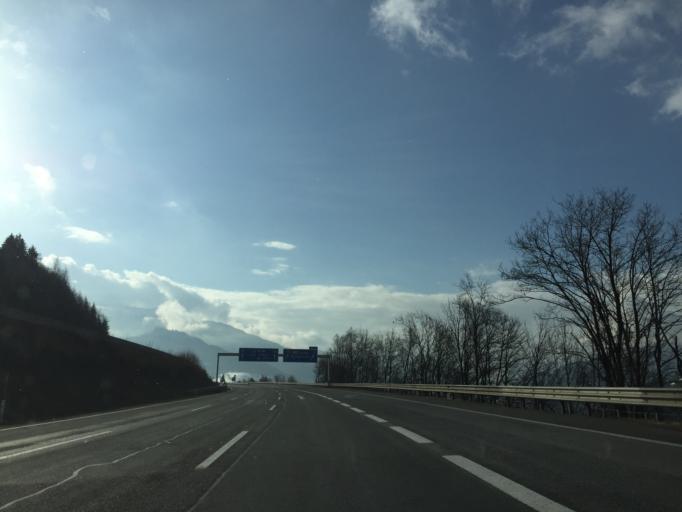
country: AT
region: Salzburg
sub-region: Politischer Bezirk Sankt Johann im Pongau
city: Pfarrwerfen
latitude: 47.4452
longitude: 13.2183
